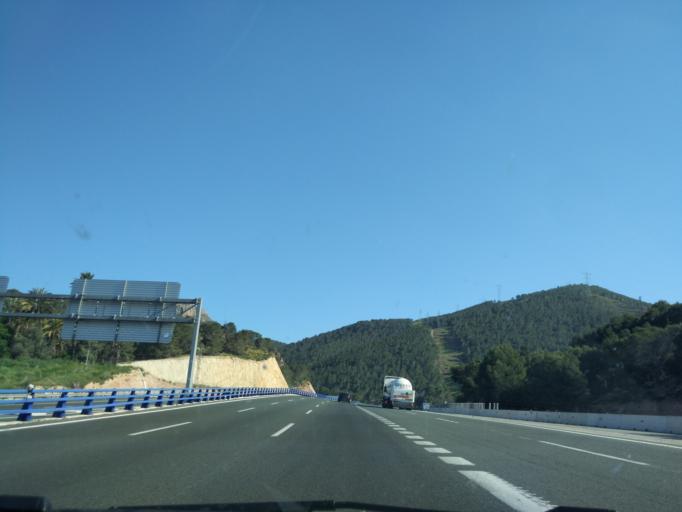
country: ES
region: Murcia
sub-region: Murcia
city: Alcantarilla
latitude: 37.9127
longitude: -1.1647
